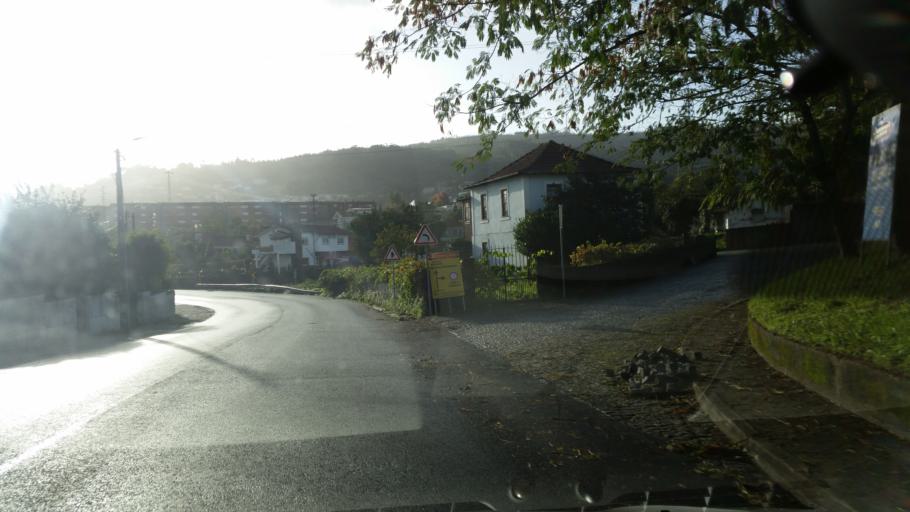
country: PT
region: Porto
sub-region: Santo Tirso
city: Aves
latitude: 41.3557
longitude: -8.4292
